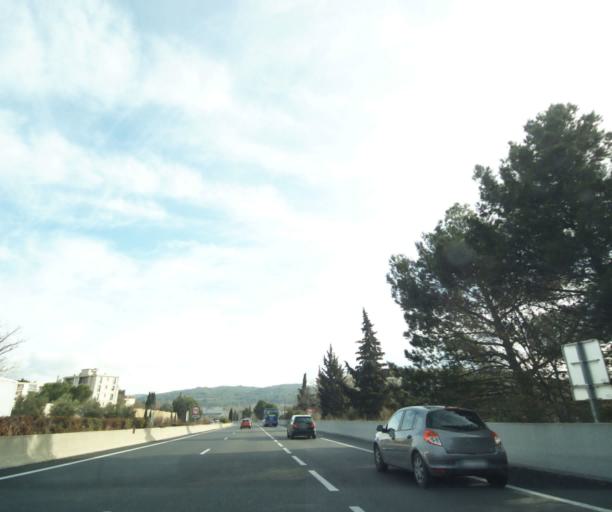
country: FR
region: Provence-Alpes-Cote d'Azur
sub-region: Departement des Bouches-du-Rhone
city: Aix-en-Provence
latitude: 43.5150
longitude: 5.4346
